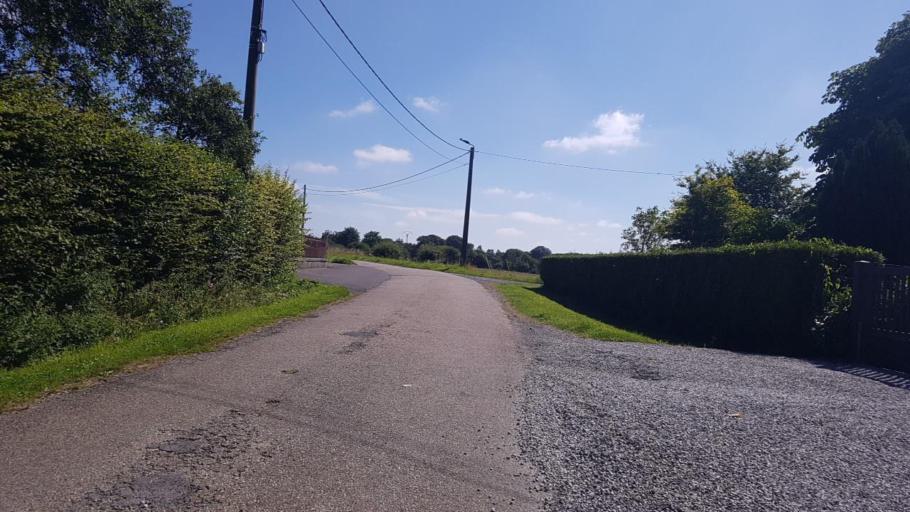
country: BE
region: Wallonia
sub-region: Province du Hainaut
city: Momignies
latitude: 50.0087
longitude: 4.1453
